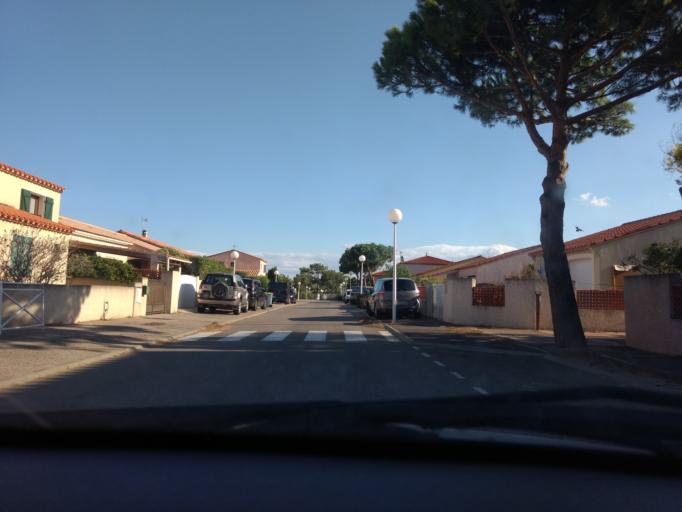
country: FR
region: Languedoc-Roussillon
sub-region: Departement des Pyrenees-Orientales
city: Le Barcares
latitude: 42.8073
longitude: 3.0332
